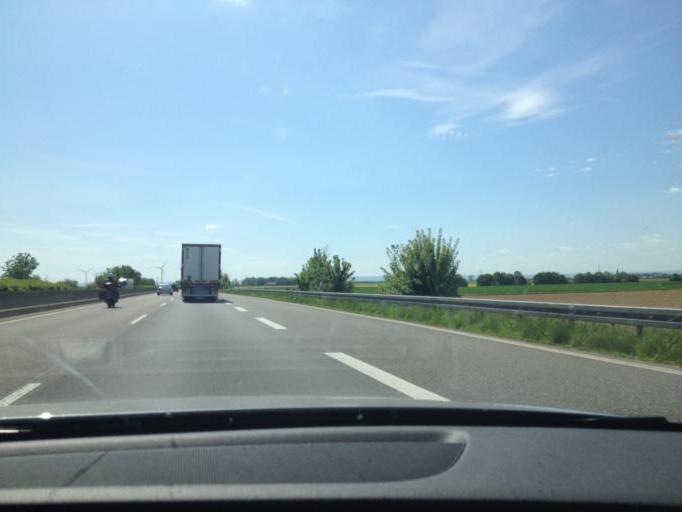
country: DE
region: North Rhine-Westphalia
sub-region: Regierungsbezirk Koln
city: Weilerswist
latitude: 50.7396
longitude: 6.7976
